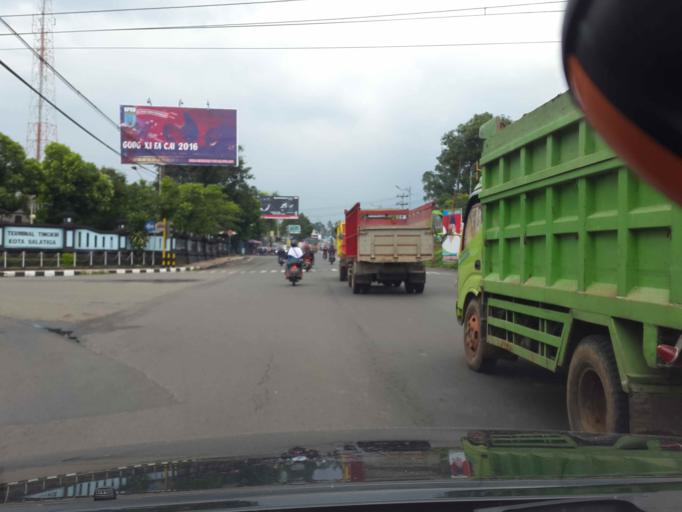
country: ID
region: Central Java
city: Salatiga
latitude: -7.3615
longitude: 110.5136
